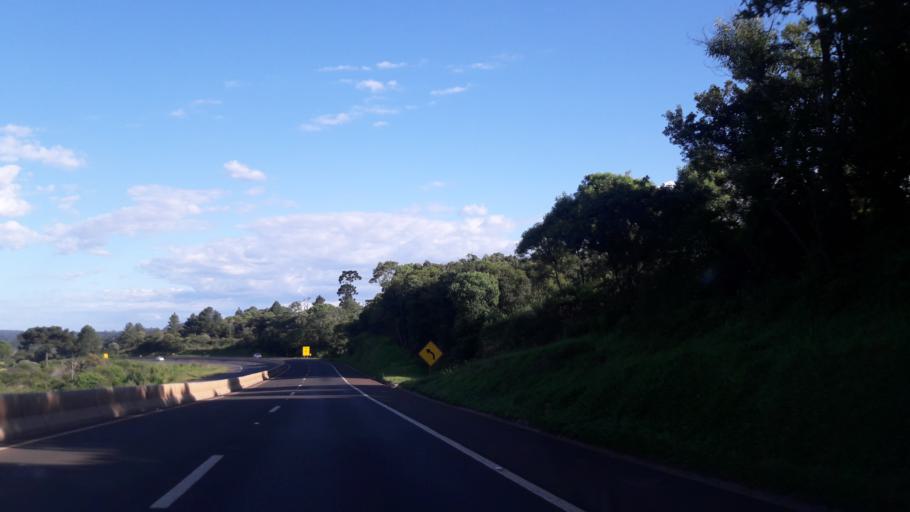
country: BR
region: Parana
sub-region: Guarapuava
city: Guarapuava
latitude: -25.3518
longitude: -51.3758
